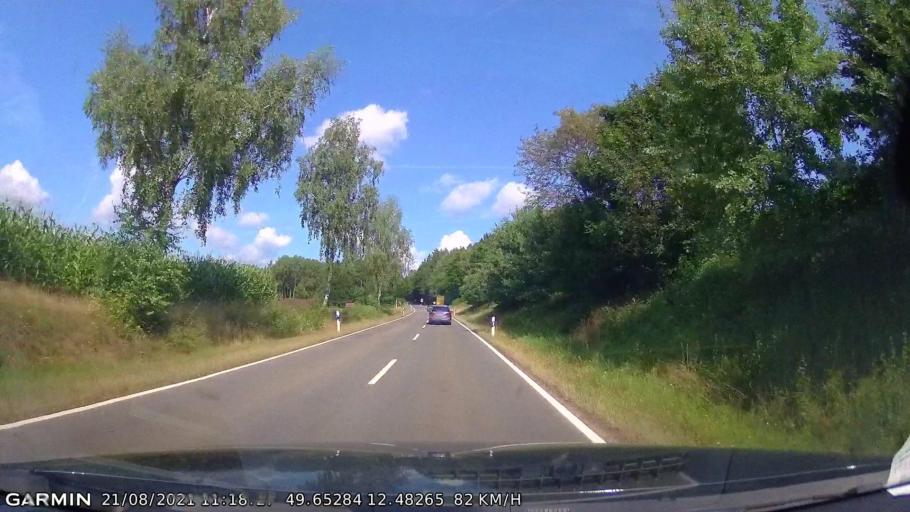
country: DE
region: Bavaria
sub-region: Upper Palatinate
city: Waidhaus
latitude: 49.6530
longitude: 12.4825
